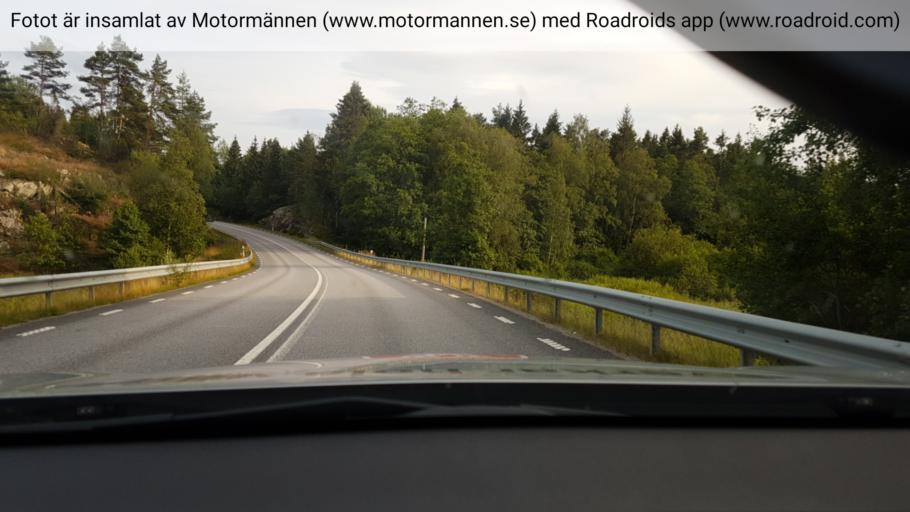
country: SE
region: Vaestra Goetaland
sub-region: Uddevalla Kommun
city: Uddevalla
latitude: 58.3971
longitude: 11.9925
